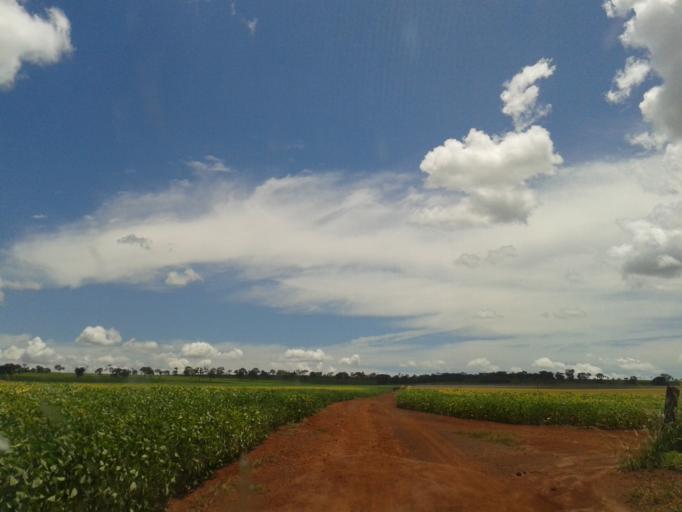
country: BR
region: Minas Gerais
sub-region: Capinopolis
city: Capinopolis
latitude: -18.7697
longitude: -49.7968
